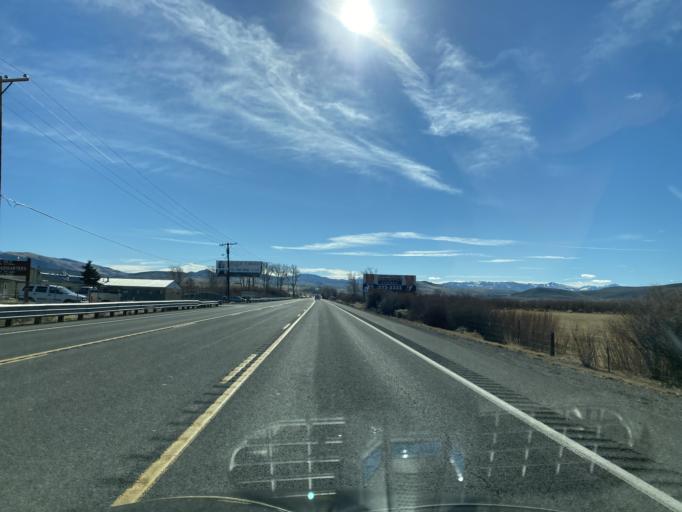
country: US
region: Nevada
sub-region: Douglas County
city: Gardnerville Ranchos
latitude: 38.9052
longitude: -119.7063
